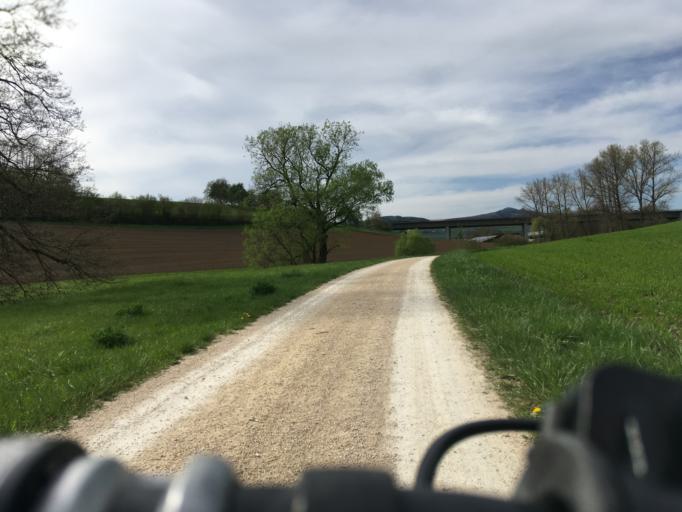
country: DE
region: Baden-Wuerttemberg
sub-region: Freiburg Region
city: Hilzingen
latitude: 47.7536
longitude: 8.7909
